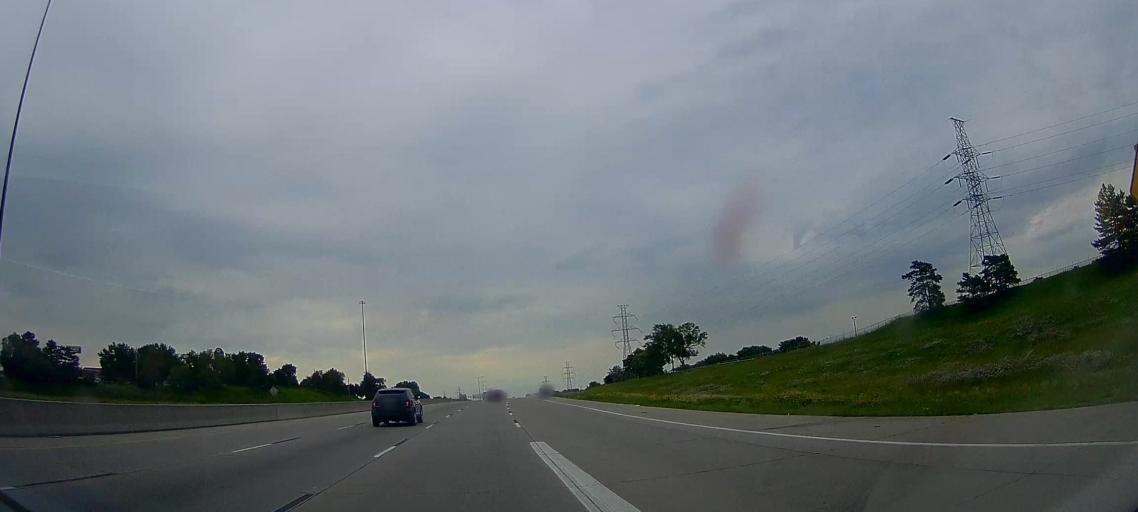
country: US
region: Nebraska
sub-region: Douglas County
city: Ralston
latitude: 41.2874
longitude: -96.0750
